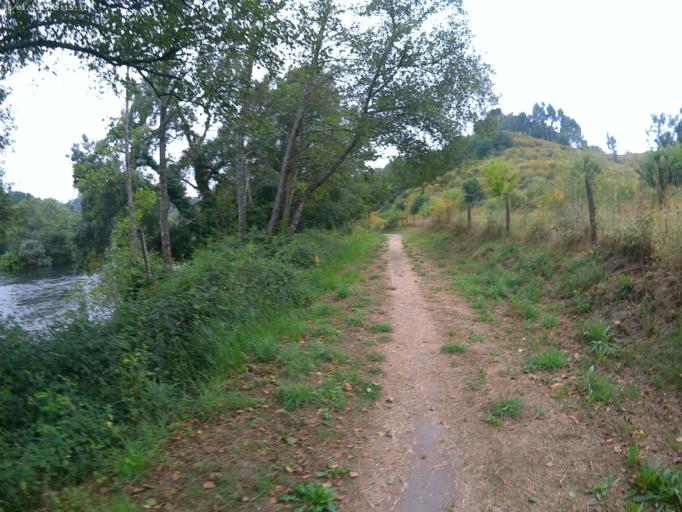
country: PT
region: Viana do Castelo
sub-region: Ponte da Barca
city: Ponte da Barca
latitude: 41.8050
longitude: -8.4546
